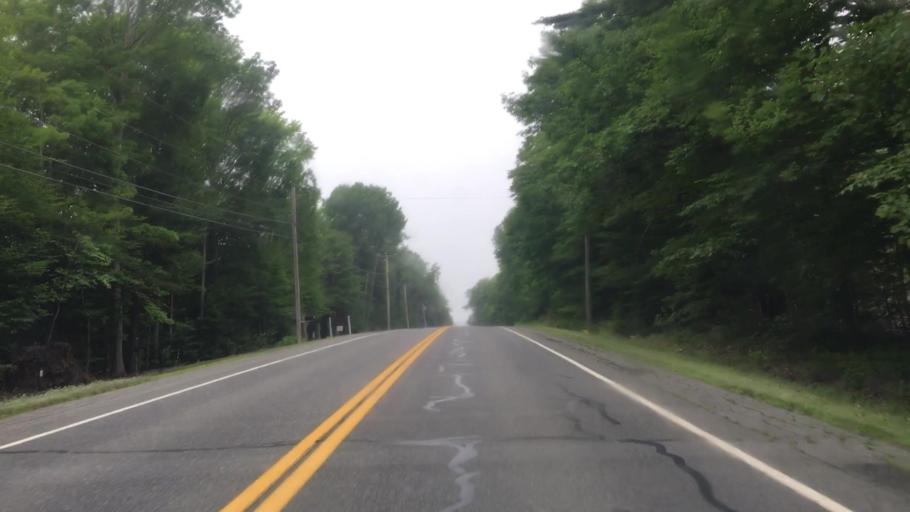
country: US
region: Maine
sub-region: Lincoln County
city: Wiscasset
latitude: 44.0666
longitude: -69.6917
